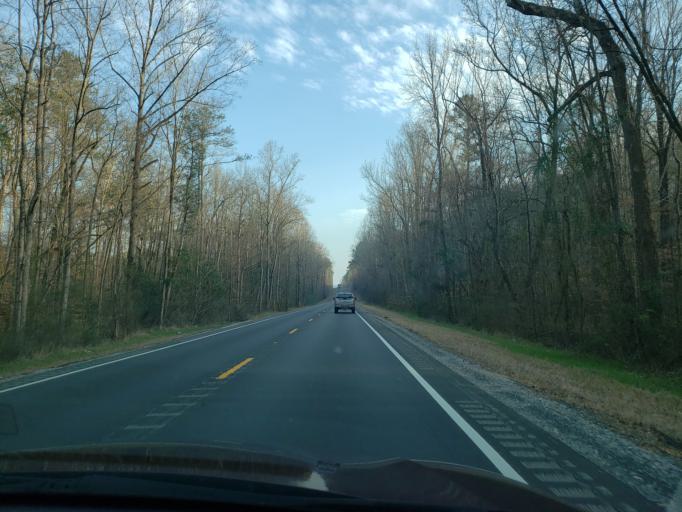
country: US
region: Alabama
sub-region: Hale County
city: Greensboro
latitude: 32.8446
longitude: -87.6098
